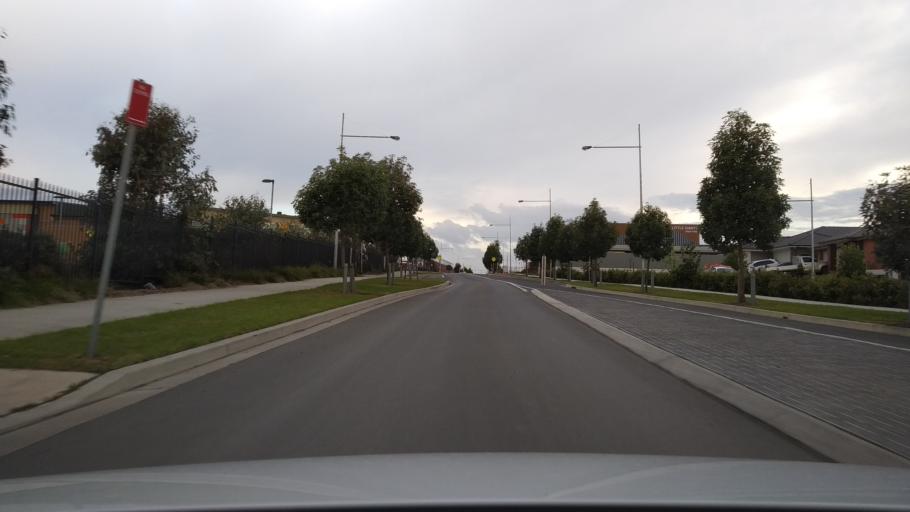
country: AU
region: New South Wales
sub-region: Camden
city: Narellan
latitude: -33.9961
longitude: 150.7347
